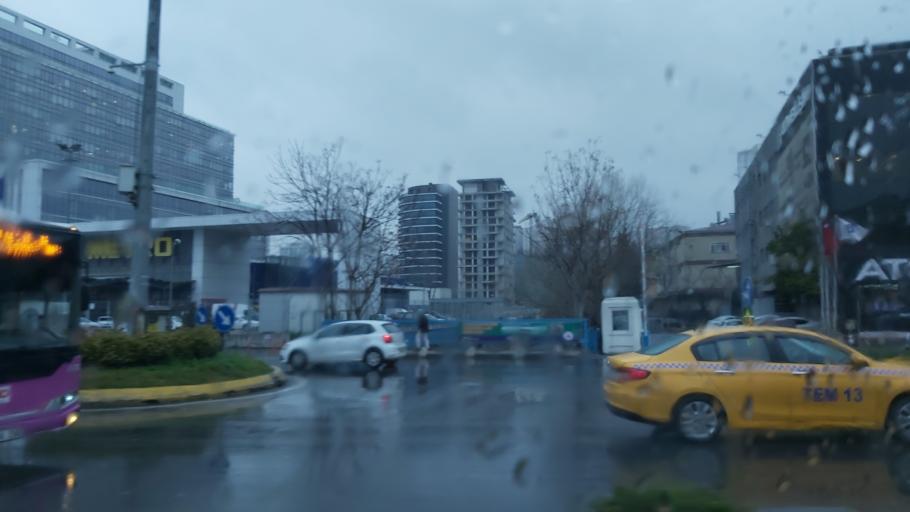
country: TR
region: Istanbul
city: Sisli
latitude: 41.0834
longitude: 28.9842
